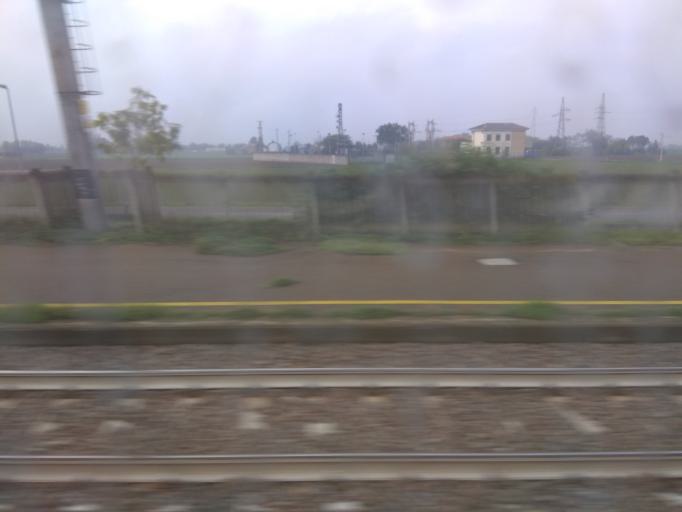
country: IT
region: Piedmont
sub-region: Provincia di Alessandria
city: Pontecurone
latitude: 44.9636
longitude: 8.9305
